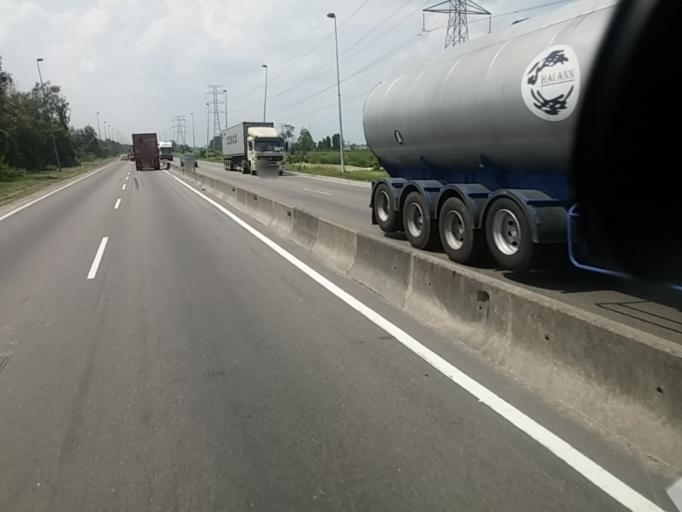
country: MY
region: Selangor
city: Klang
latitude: 2.9746
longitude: 101.3672
